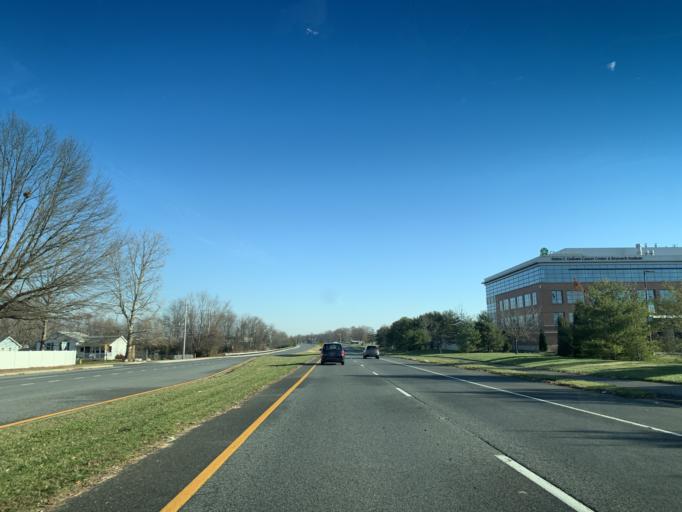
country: US
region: Delaware
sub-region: New Castle County
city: Pike Creek
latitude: 39.6879
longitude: -75.6771
